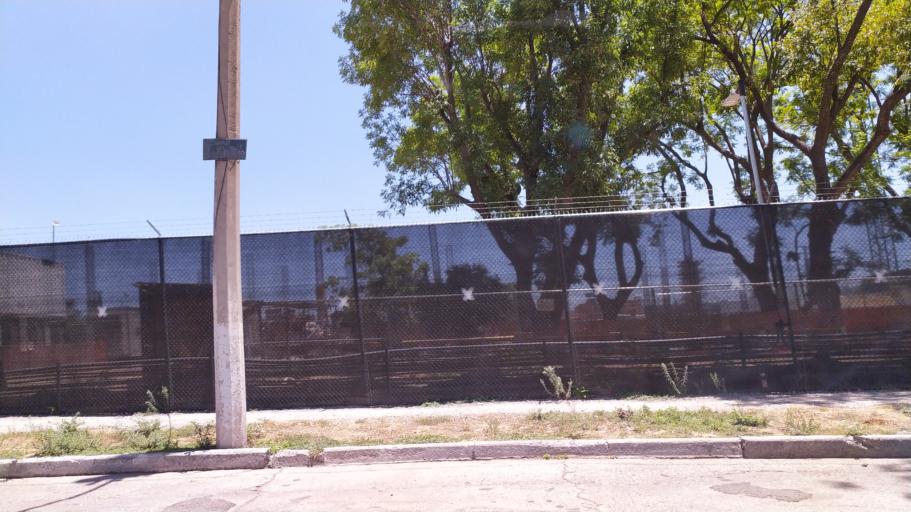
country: MX
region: Jalisco
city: Guadalajara
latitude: 20.6848
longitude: -103.3972
